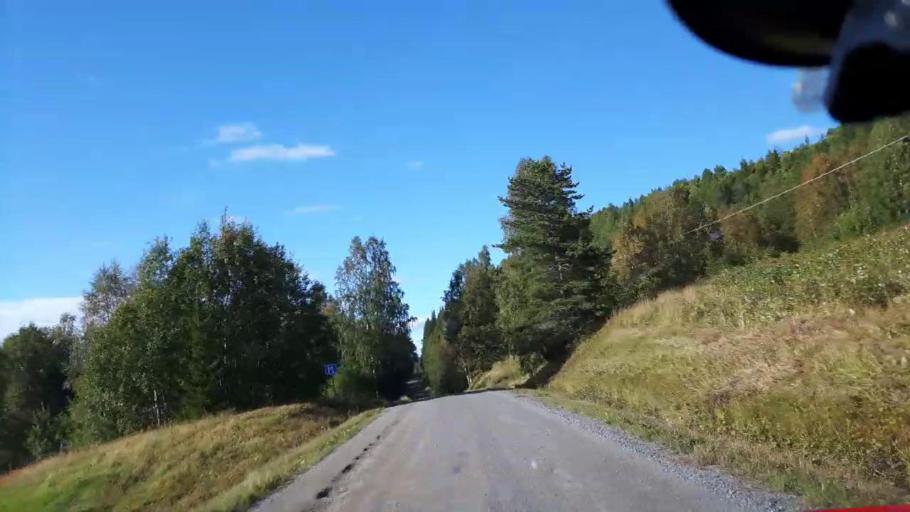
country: SE
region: Jaemtland
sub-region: Ragunda Kommun
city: Hammarstrand
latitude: 63.4968
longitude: 16.0371
